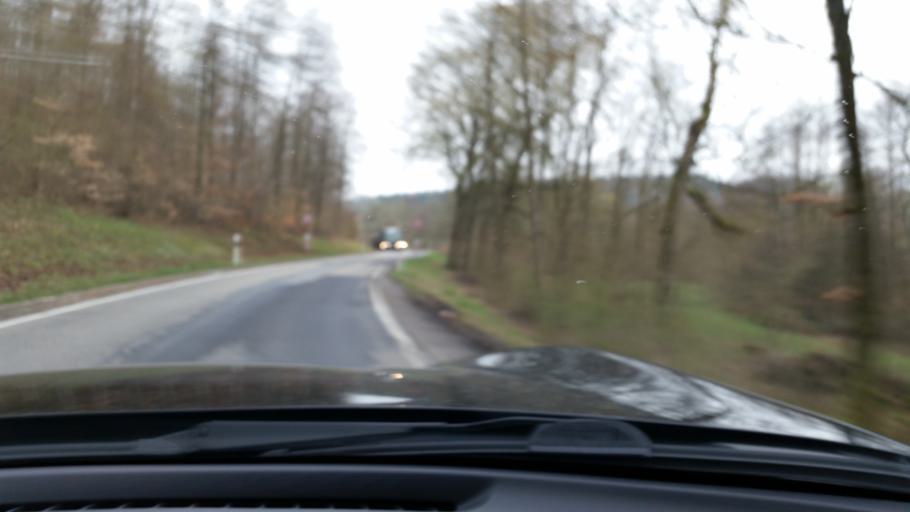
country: DE
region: Baden-Wuerttemberg
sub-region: Karlsruhe Region
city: Seckach
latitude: 49.4598
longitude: 9.3342
